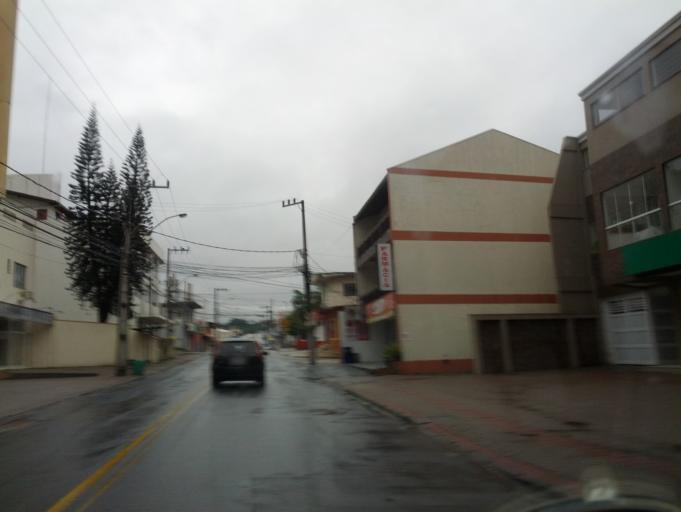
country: BR
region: Santa Catarina
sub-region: Blumenau
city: Blumenau
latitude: -26.9109
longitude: -49.0936
